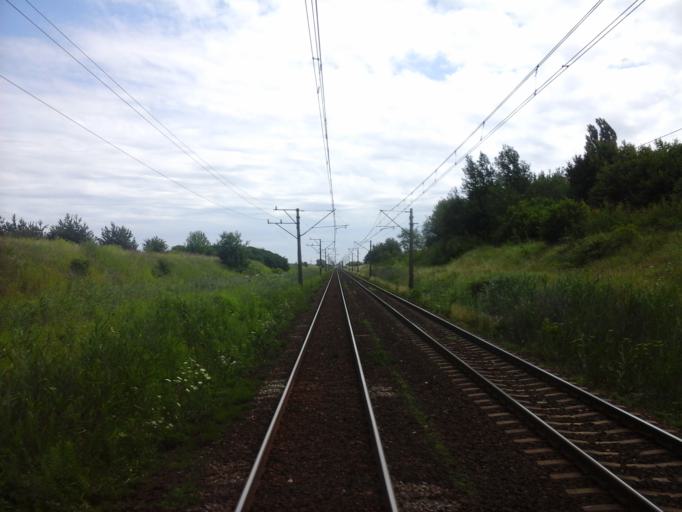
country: PL
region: West Pomeranian Voivodeship
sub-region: Powiat stargardzki
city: Stargard Szczecinski
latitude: 53.3573
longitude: 14.9800
